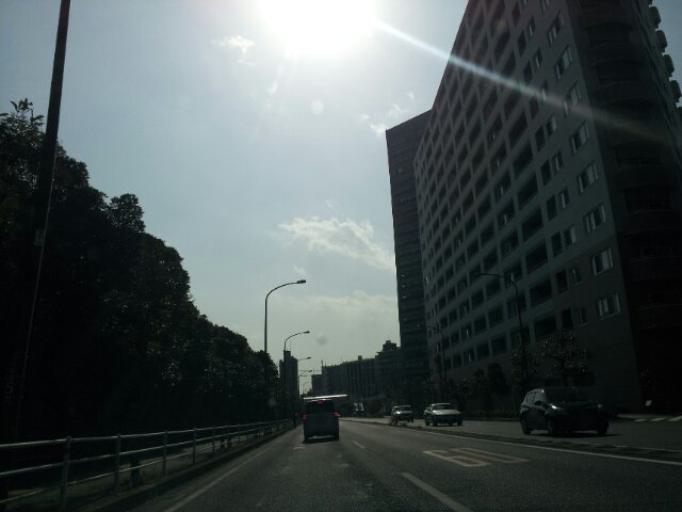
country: JP
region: Kanagawa
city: Yokohama
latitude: 35.4805
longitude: 139.6348
